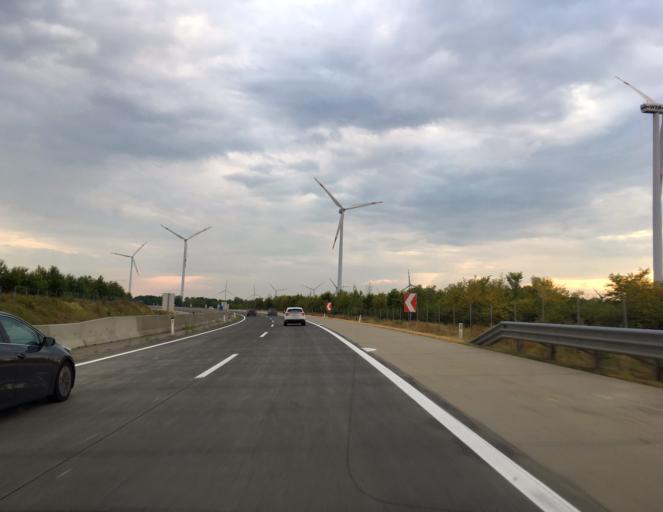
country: AT
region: Burgenland
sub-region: Politischer Bezirk Neusiedl am See
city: Potzneusiedl
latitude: 48.0404
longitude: 16.9003
